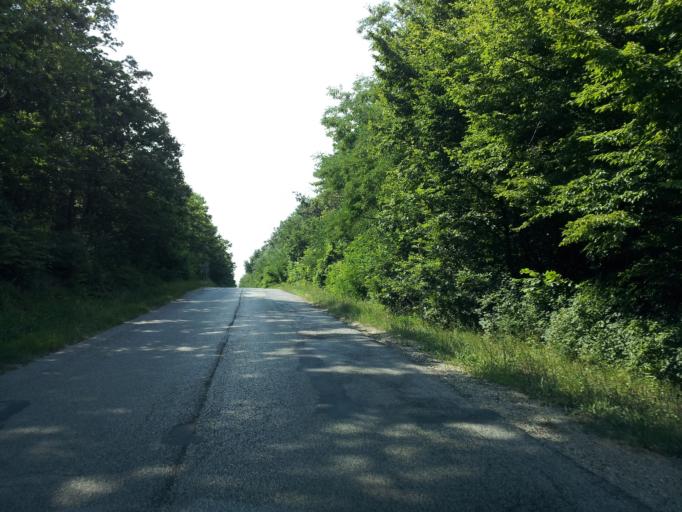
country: HU
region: Veszprem
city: Balatonfured
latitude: 46.9638
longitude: 17.8552
